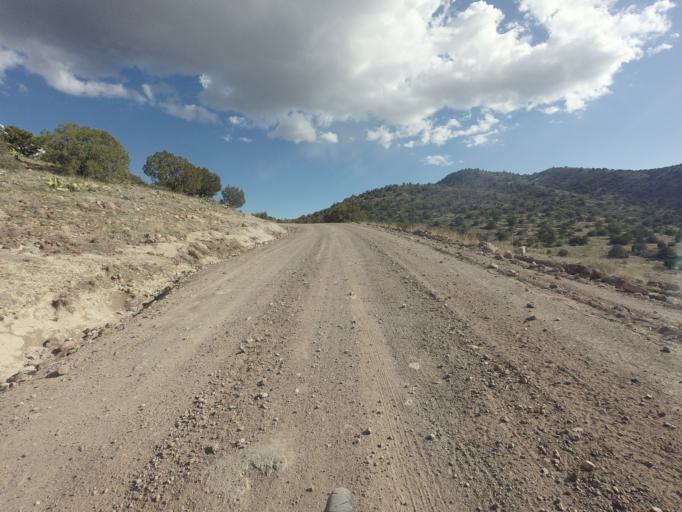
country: US
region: Arizona
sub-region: Gila County
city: Pine
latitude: 34.4266
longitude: -111.6756
